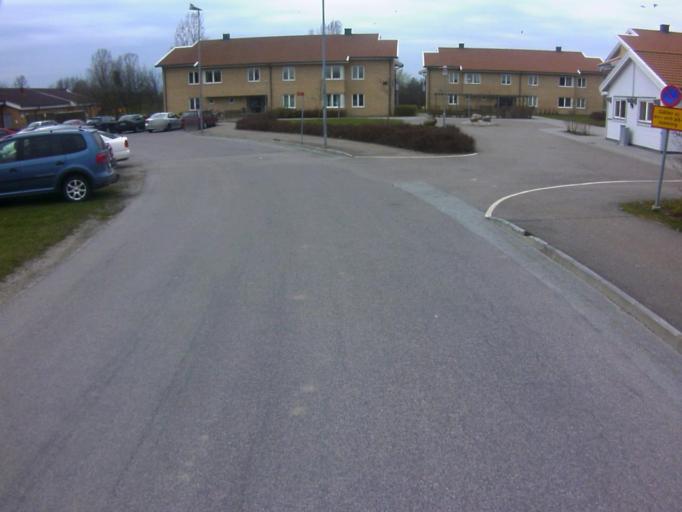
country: SE
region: Skane
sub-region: Kavlinge Kommun
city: Kaevlinge
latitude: 55.7947
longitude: 13.0946
